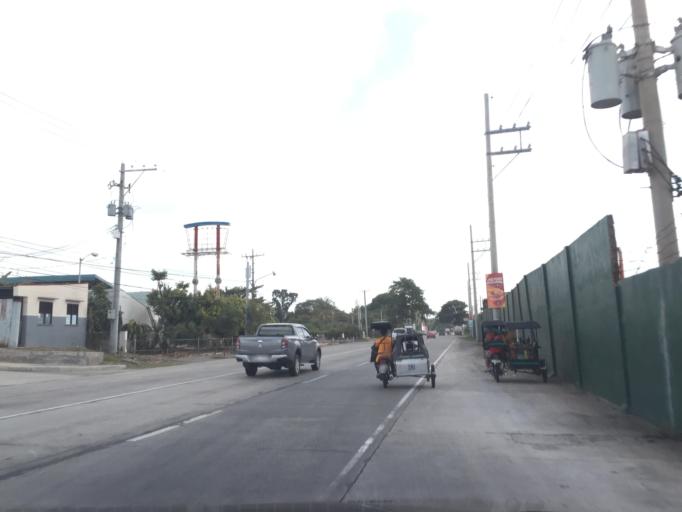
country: PH
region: Central Luzon
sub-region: Province of Tarlac
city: Salcedo
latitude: 15.8707
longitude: 120.6033
